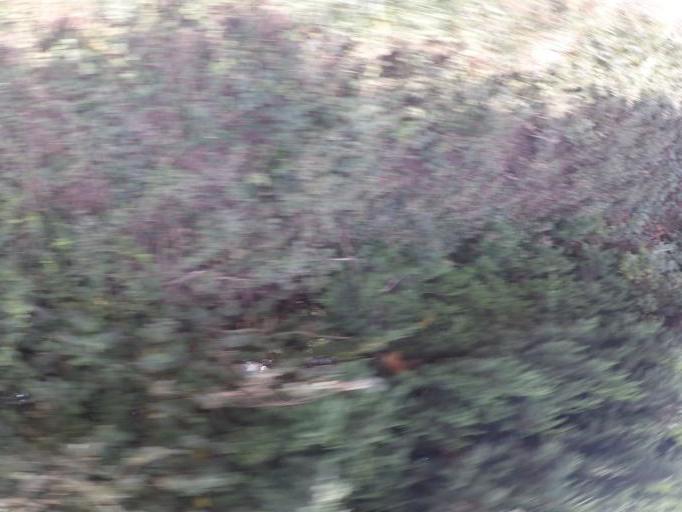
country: FR
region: Brittany
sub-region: Departement des Cotes-d'Armor
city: Tremuson
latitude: 48.5407
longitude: -2.8920
